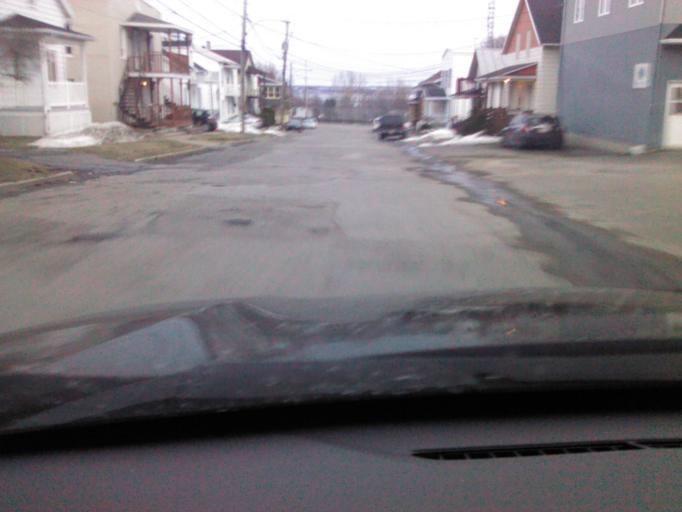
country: CA
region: Quebec
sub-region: Capitale-Nationale
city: Donnacona
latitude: 46.6740
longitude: -71.7361
